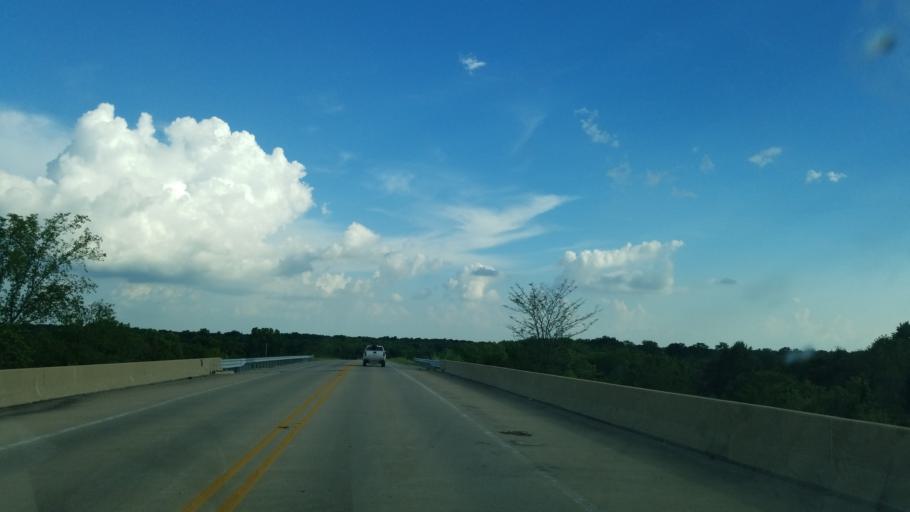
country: US
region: Illinois
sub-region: Marion County
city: Sandoval
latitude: 38.5806
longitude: -89.1084
